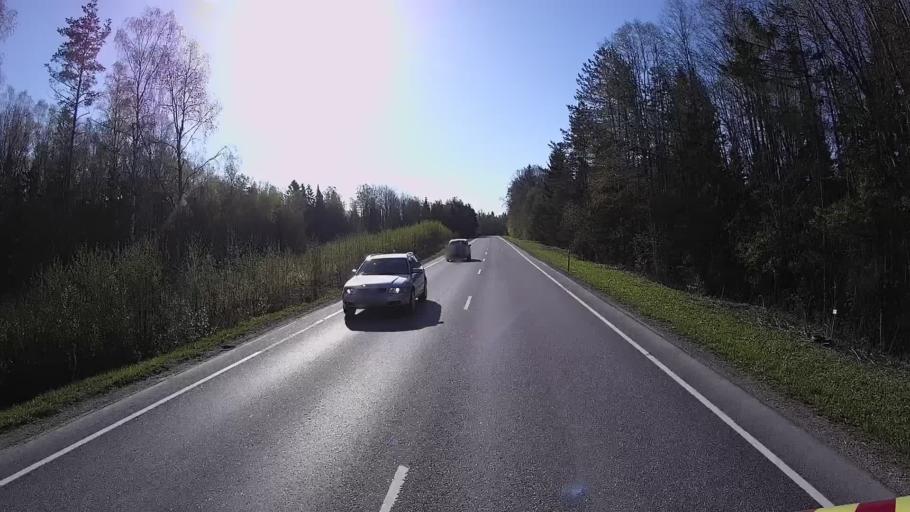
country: EE
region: Raplamaa
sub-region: Kehtna vald
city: Kehtna
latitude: 58.8843
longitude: 24.9697
